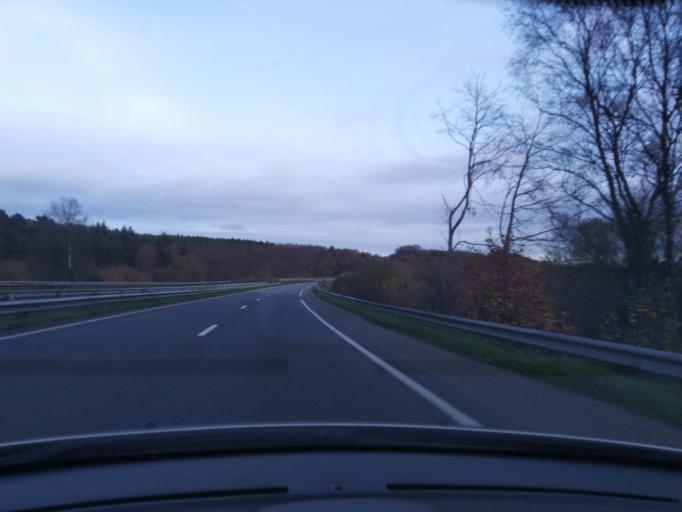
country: FR
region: Brittany
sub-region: Departement du Finistere
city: Plouigneau
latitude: 48.5786
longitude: -3.6467
